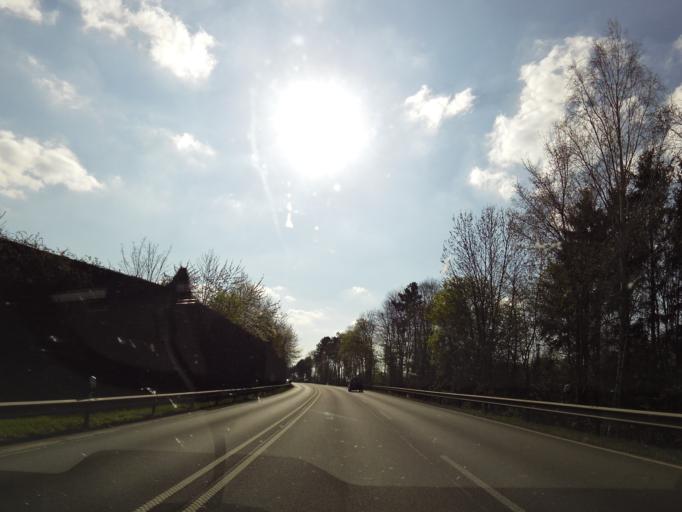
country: DE
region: North Rhine-Westphalia
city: Porta Westfalica
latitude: 52.2334
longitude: 8.9023
